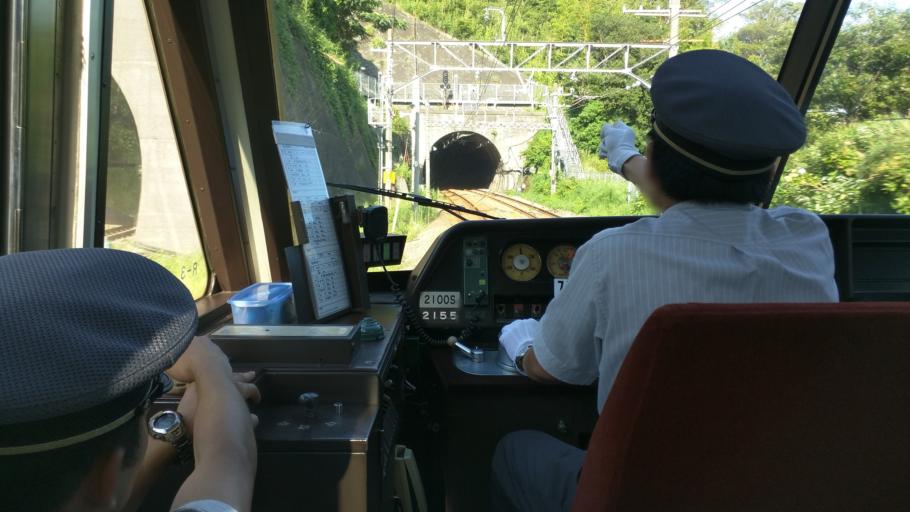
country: JP
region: Shizuoka
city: Atami
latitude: 35.0994
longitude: 139.0697
